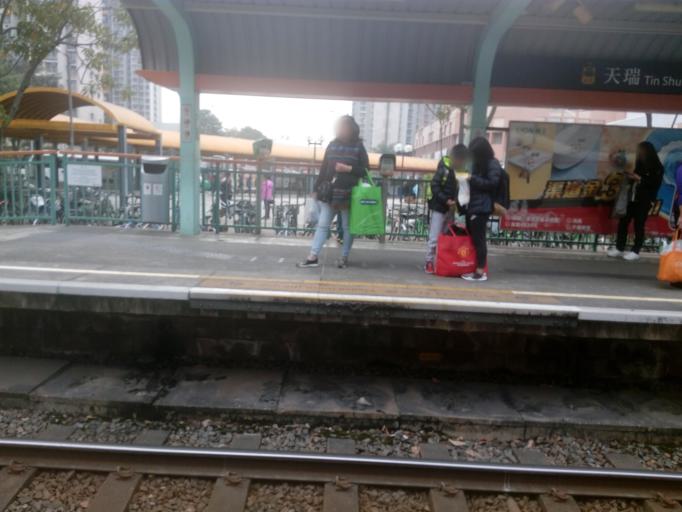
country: HK
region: Yuen Long
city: Yuen Long Kau Hui
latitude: 22.4559
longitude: 113.9997
